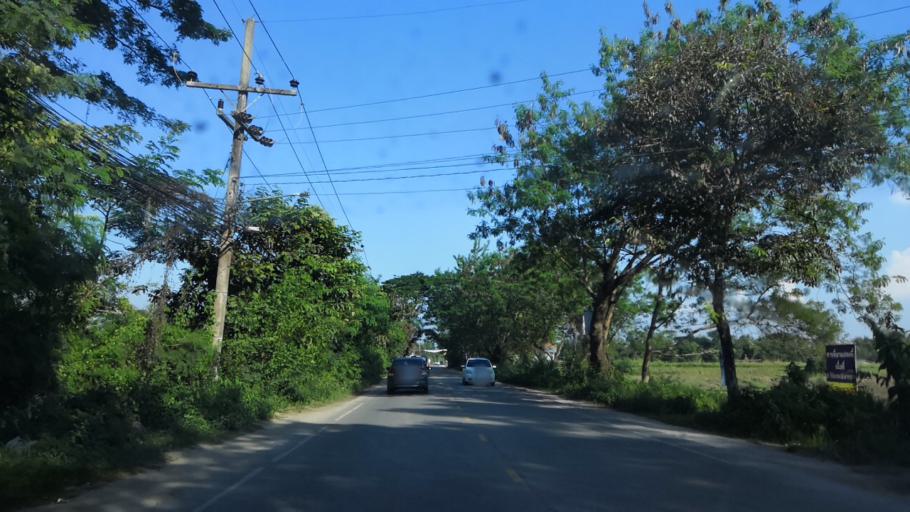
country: TH
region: Chiang Rai
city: Chiang Rai
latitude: 19.9291
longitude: 99.8552
